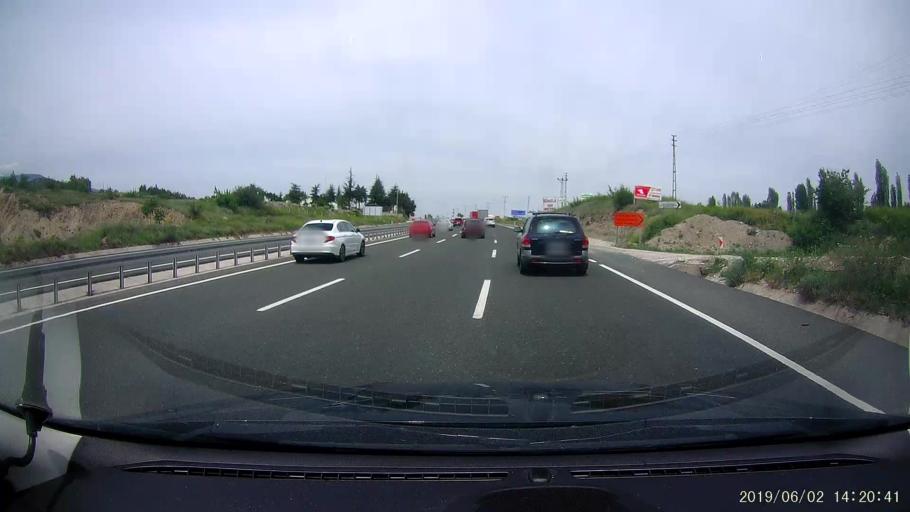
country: TR
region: Kastamonu
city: Tosya
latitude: 40.9720
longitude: 33.9957
